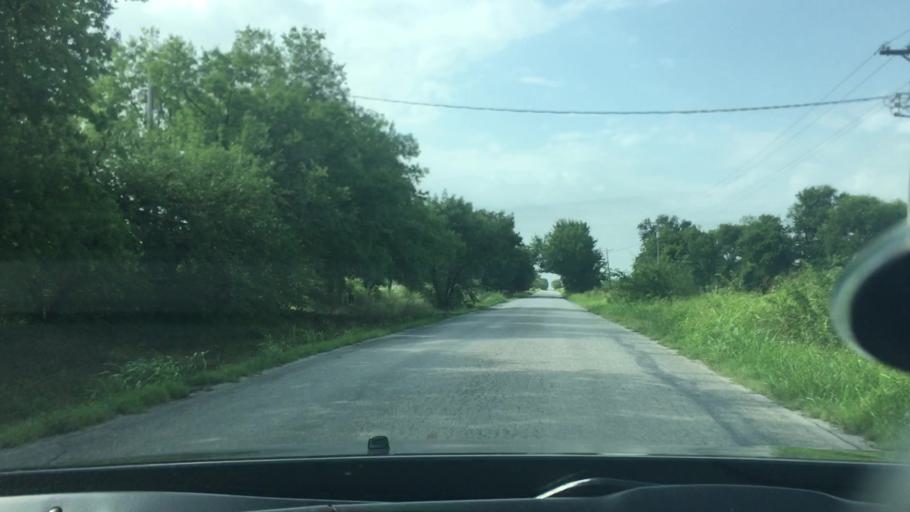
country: US
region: Oklahoma
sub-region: Carter County
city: Lone Grove
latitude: 34.2134
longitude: -97.2650
